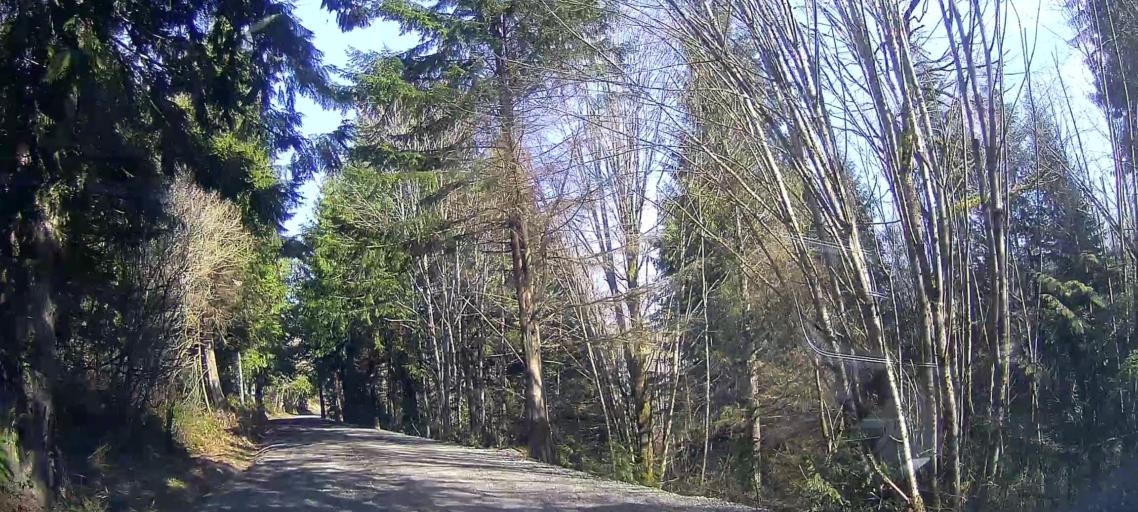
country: US
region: Washington
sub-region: Skagit County
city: Burlington
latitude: 48.5876
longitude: -122.3863
